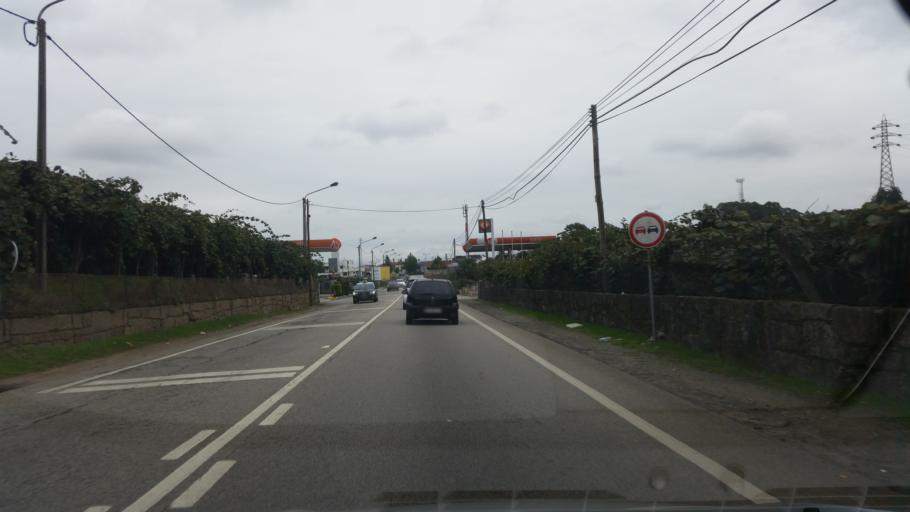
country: PT
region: Porto
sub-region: Valongo
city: Ermesinde
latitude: 41.2330
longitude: -8.5489
